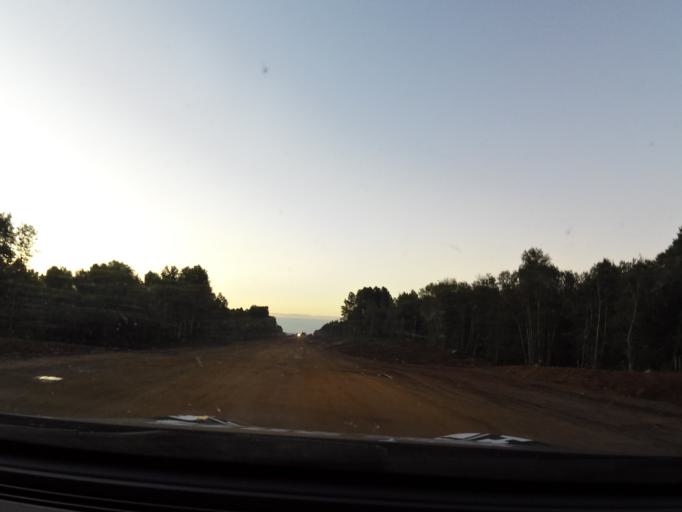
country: RU
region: Vologda
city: Vytegra
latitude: 60.9946
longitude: 36.1190
